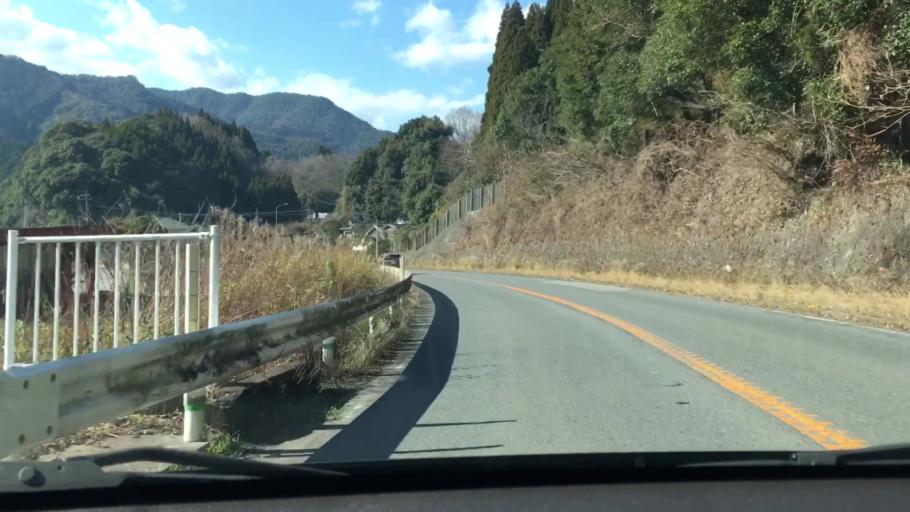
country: JP
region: Oita
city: Saiki
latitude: 32.9890
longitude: 131.8358
